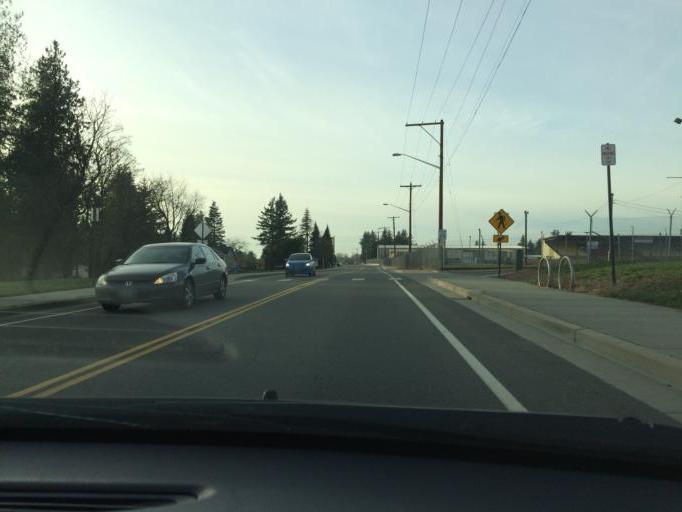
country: US
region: Washington
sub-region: Whatcom County
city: Lynden
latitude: 48.9357
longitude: -122.4716
